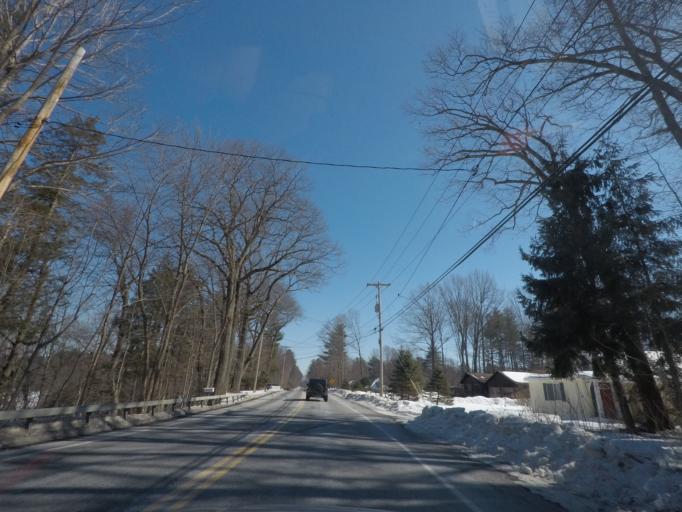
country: US
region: New York
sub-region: Saratoga County
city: Saratoga Springs
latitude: 43.0507
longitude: -73.7418
